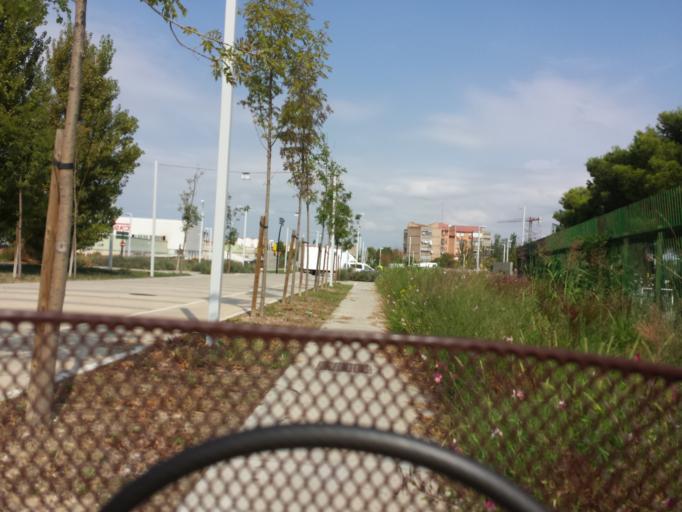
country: ES
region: Aragon
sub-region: Provincia de Zaragoza
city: Oliver-Valdefierro, Oliver, Valdefierro
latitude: 41.6447
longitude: -0.9239
